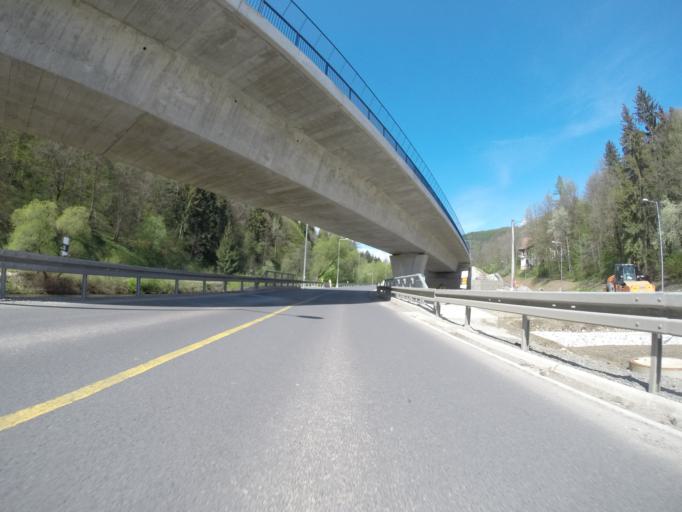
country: SK
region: Banskobystricky
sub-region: Okres Banska Bystrica
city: Brezno
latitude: 48.8064
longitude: 19.6168
